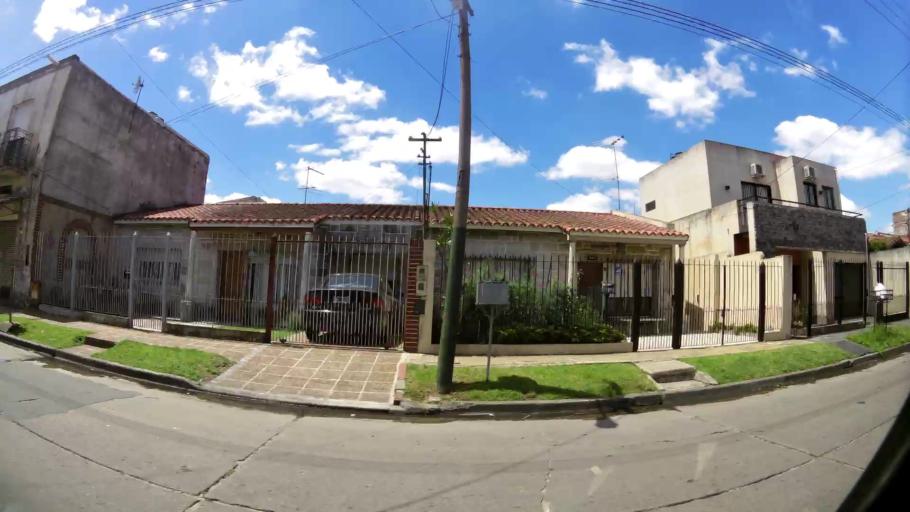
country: AR
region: Buenos Aires
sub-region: Partido de Lomas de Zamora
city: Lomas de Zamora
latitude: -34.7321
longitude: -58.4204
